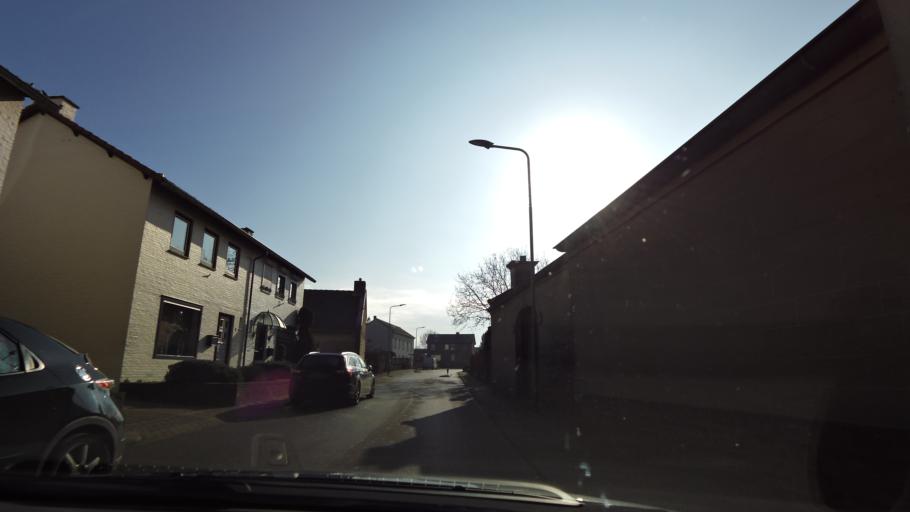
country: NL
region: Limburg
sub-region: Valkenburg aan de Geul
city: Sibbe
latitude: 50.8390
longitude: 5.8321
